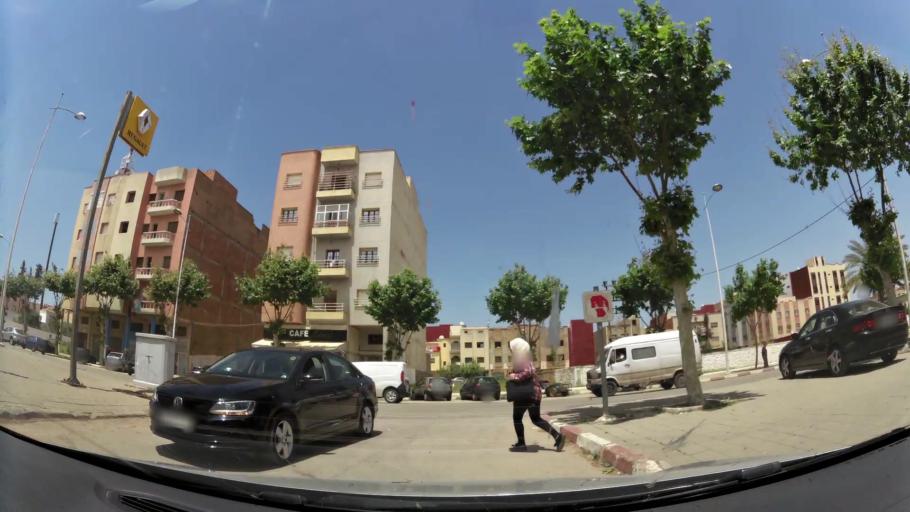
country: MA
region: Rabat-Sale-Zemmour-Zaer
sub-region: Khemisset
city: Khemisset
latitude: 33.8262
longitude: -6.0786
